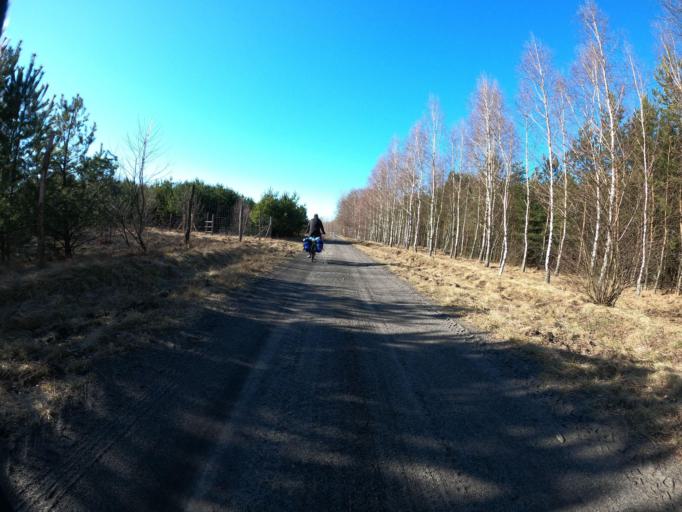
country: PL
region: West Pomeranian Voivodeship
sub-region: Powiat szczecinecki
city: Borne Sulinowo
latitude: 53.5497
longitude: 16.5505
